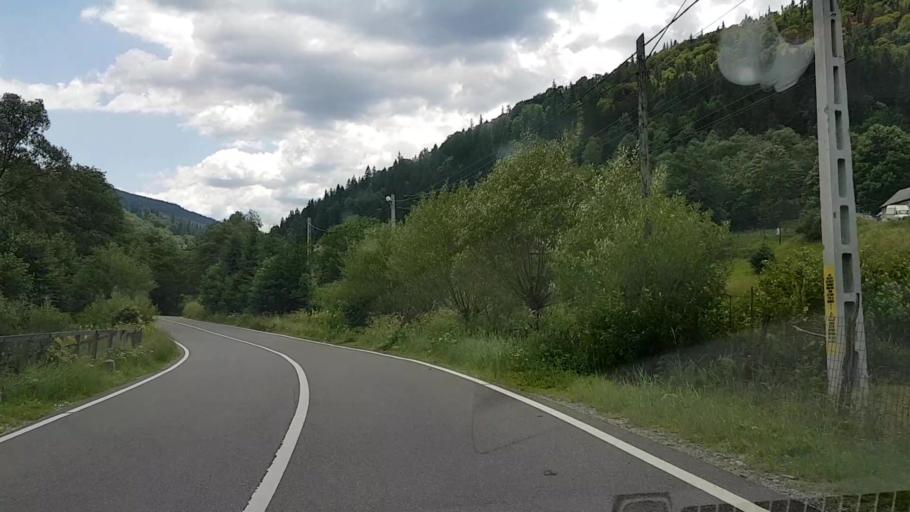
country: RO
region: Suceava
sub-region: Comuna Crucea
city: Crucea
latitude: 47.3287
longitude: 25.6201
